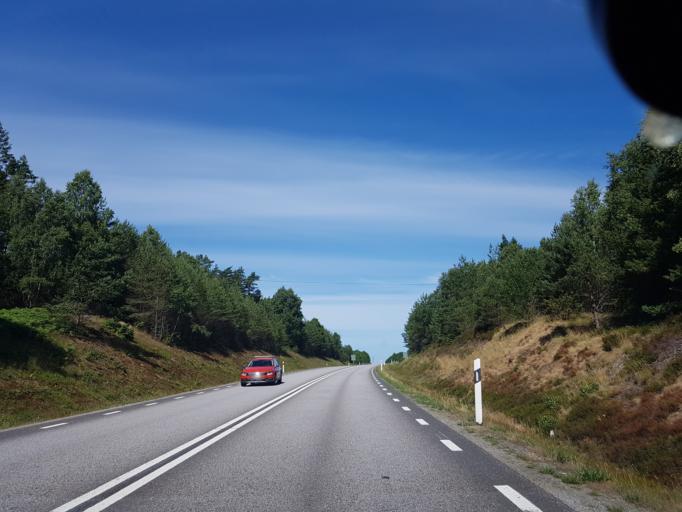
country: SE
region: Vaestra Goetaland
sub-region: Lysekils Kommun
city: Lysekil
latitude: 58.1582
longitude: 11.5035
